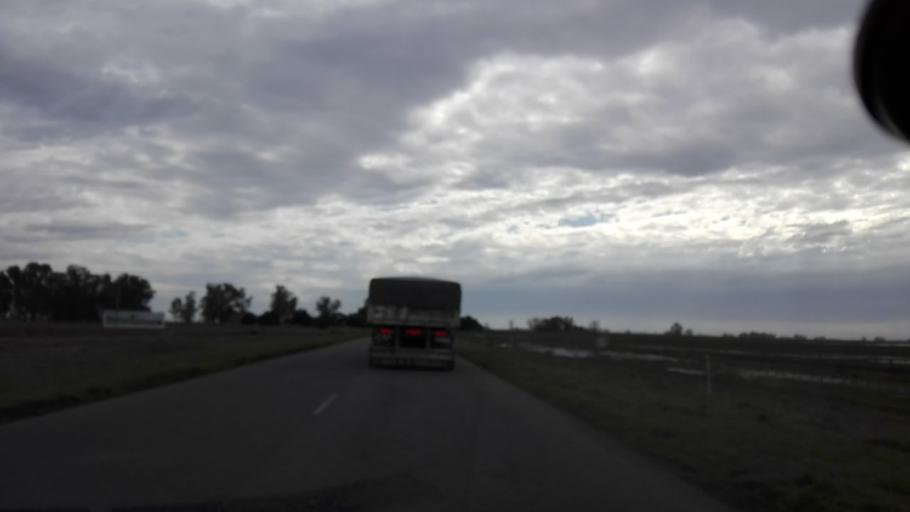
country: AR
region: Buenos Aires
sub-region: Partido de Las Flores
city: Las Flores
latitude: -36.2090
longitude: -59.0477
